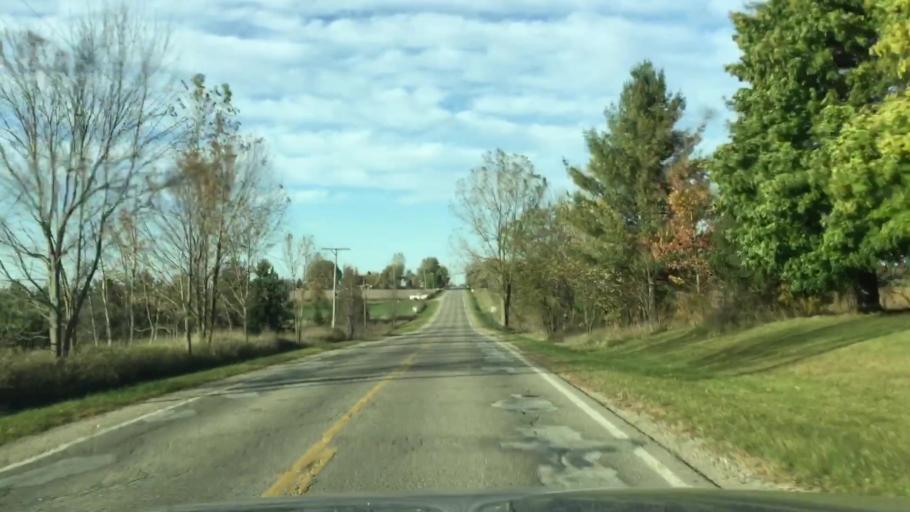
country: US
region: Michigan
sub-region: Lapeer County
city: North Branch
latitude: 43.2429
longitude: -83.1974
